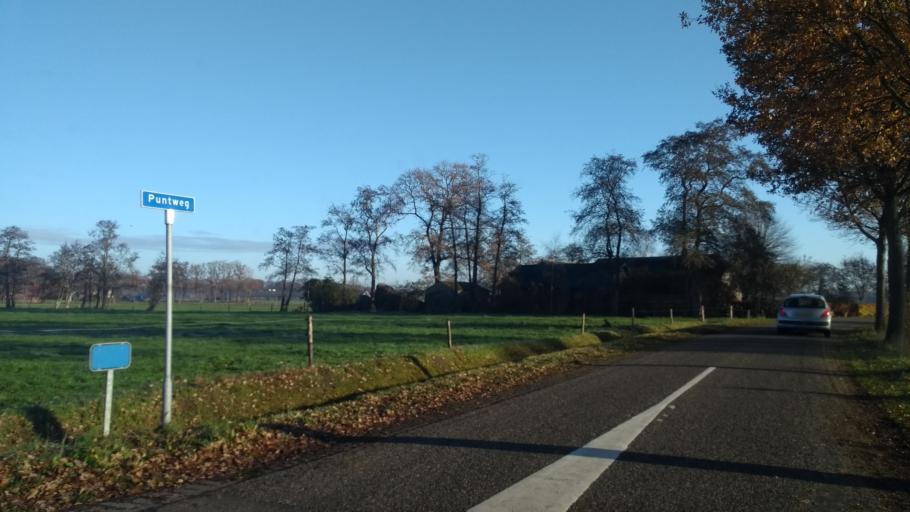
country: NL
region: Overijssel
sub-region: Gemeente Staphorst
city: Staphorst
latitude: 52.6000
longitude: 6.2822
